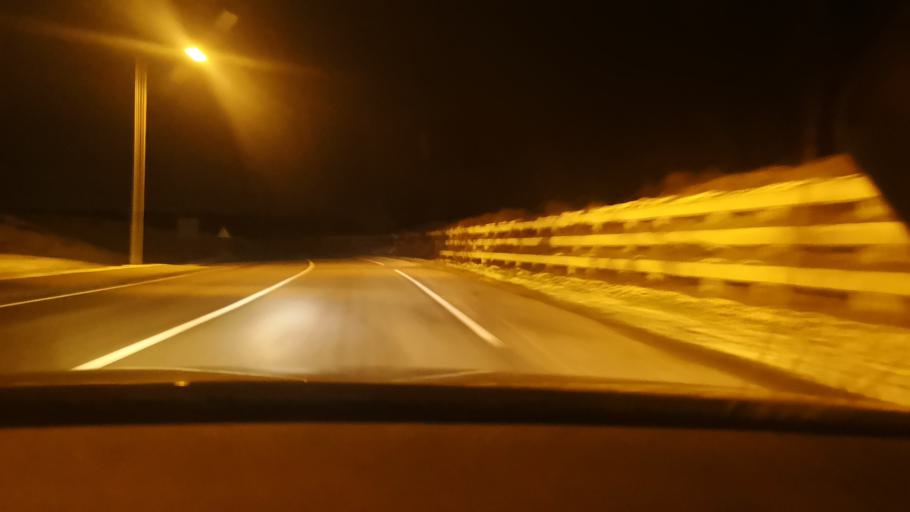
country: FR
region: Rhone-Alpes
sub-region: Departement de l'Ain
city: Montagnat
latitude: 46.2041
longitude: 5.2736
